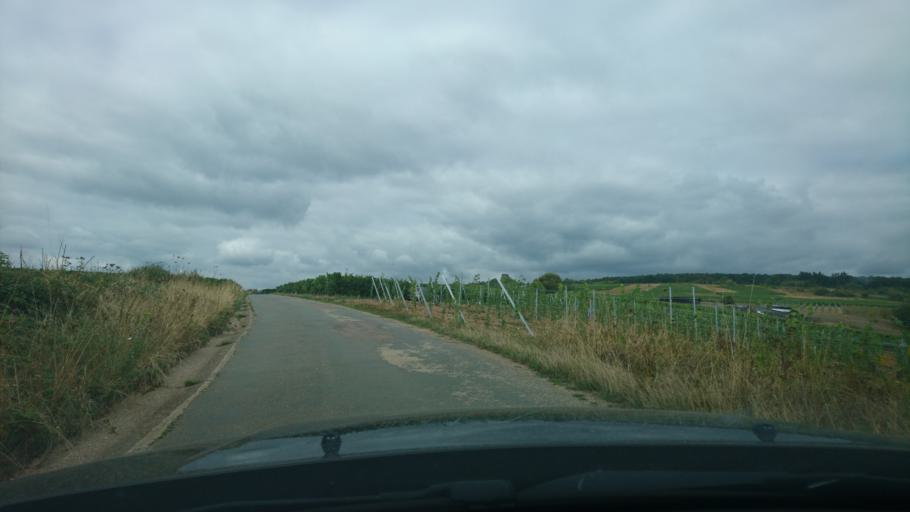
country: DE
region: Rheinland-Pfalz
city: Wiltingen
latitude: 49.6636
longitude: 6.6050
